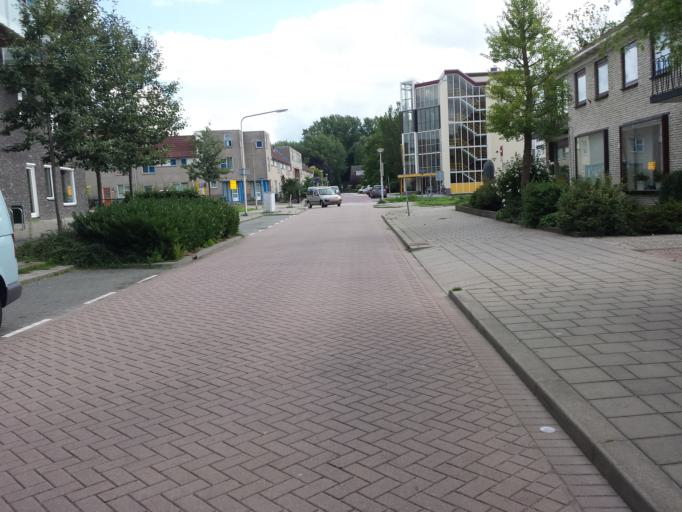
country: NL
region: South Holland
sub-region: Gemeente Gouda
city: Gouda
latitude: 52.0129
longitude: 4.7278
